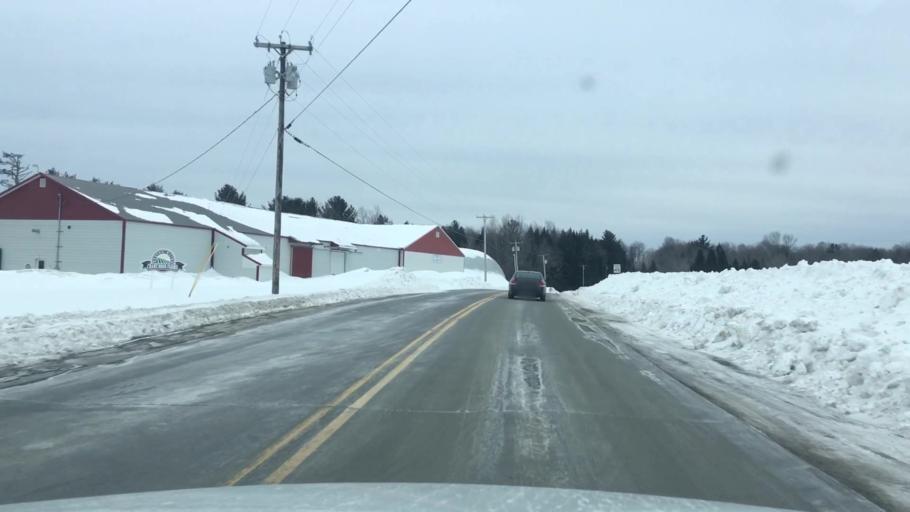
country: US
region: Maine
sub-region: Penobscot County
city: Garland
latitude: 44.9887
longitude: -69.0876
